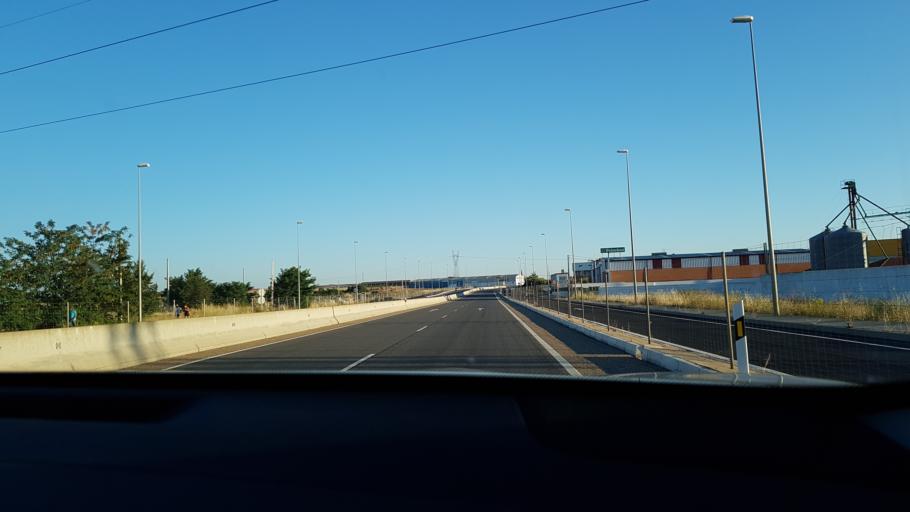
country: ES
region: Castille and Leon
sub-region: Provincia de Zamora
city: Valcabado
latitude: 41.5349
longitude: -5.7618
